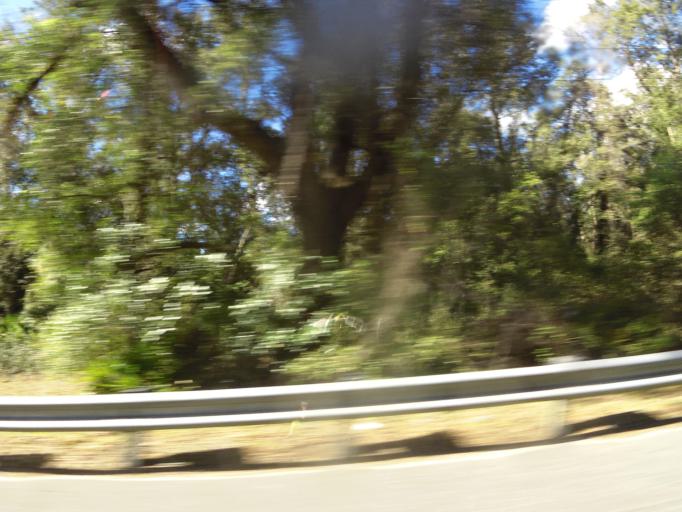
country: US
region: Florida
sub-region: Putnam County
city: Interlachen
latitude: 29.7316
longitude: -81.9103
